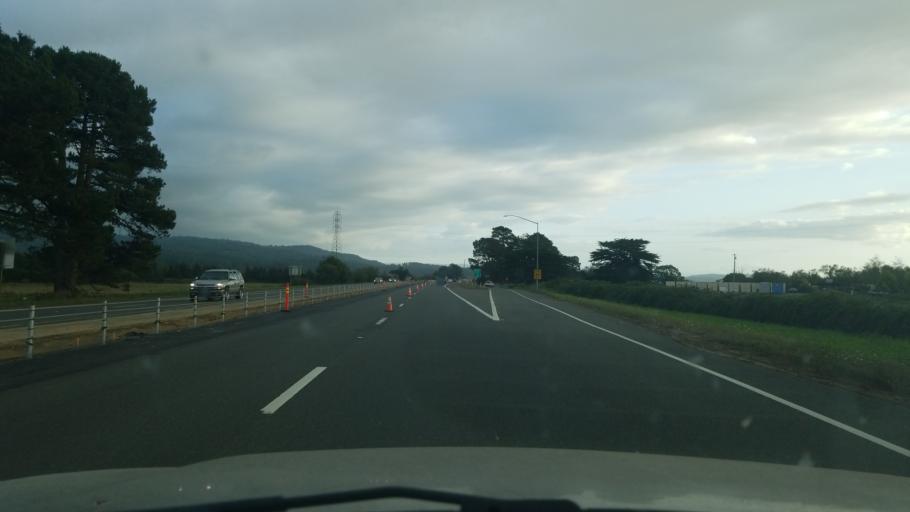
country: US
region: California
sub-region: Humboldt County
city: Arcata
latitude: 40.8537
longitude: -124.0822
